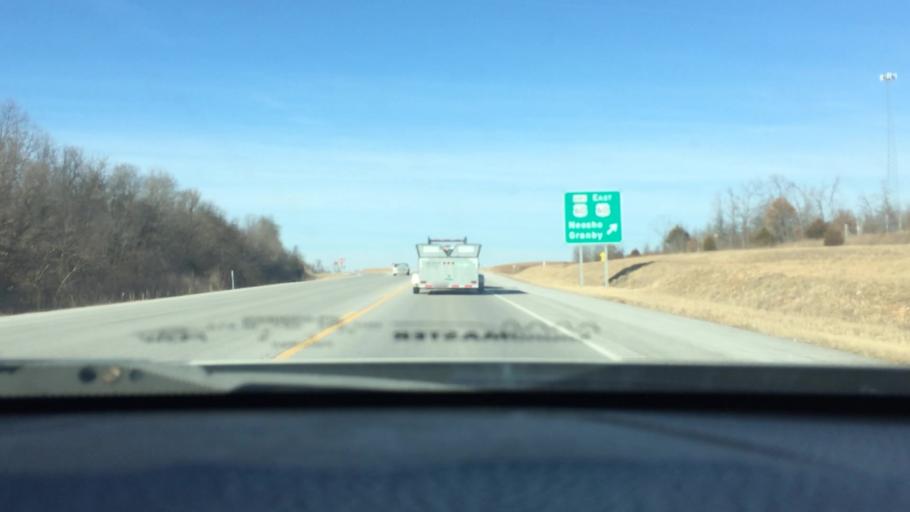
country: US
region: Missouri
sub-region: Newton County
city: Neosho
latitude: 36.8995
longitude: -94.3169
